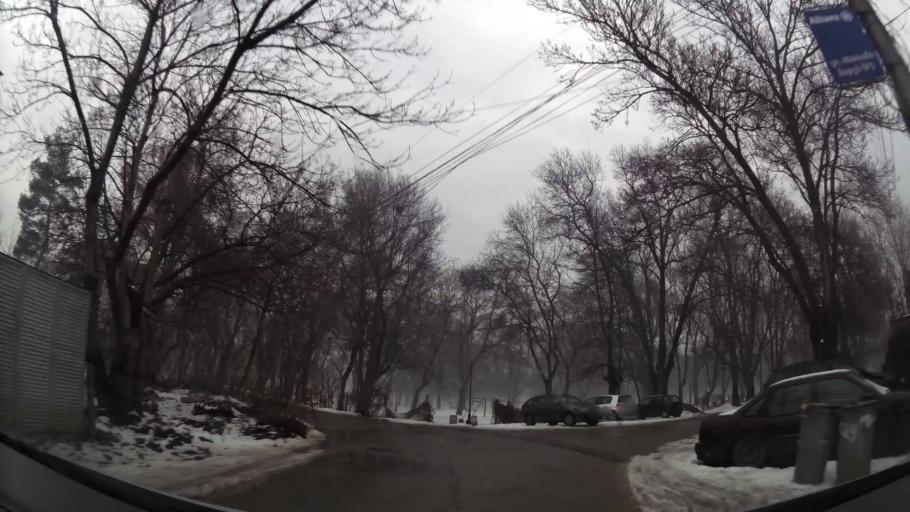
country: BG
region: Sofia-Capital
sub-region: Stolichna Obshtina
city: Sofia
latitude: 42.6780
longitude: 23.2645
